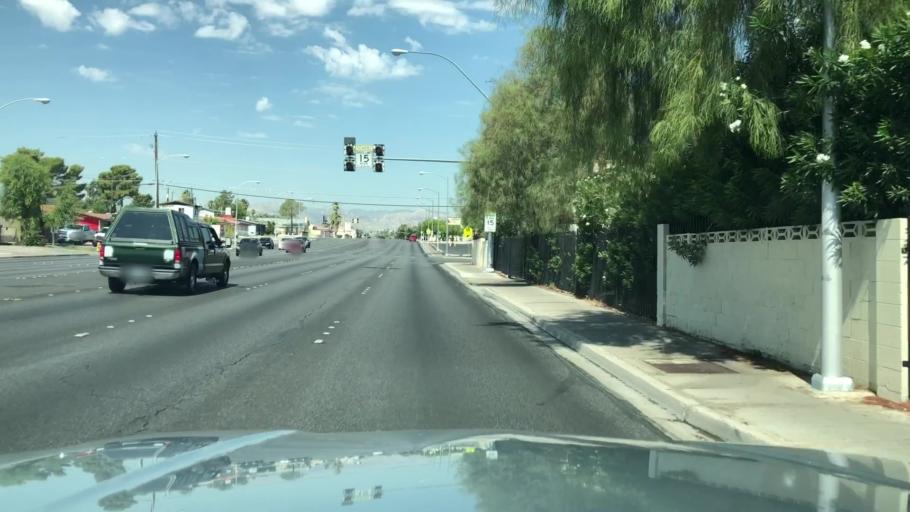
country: US
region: Nevada
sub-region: Clark County
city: Spring Valley
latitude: 36.1301
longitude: -115.2025
